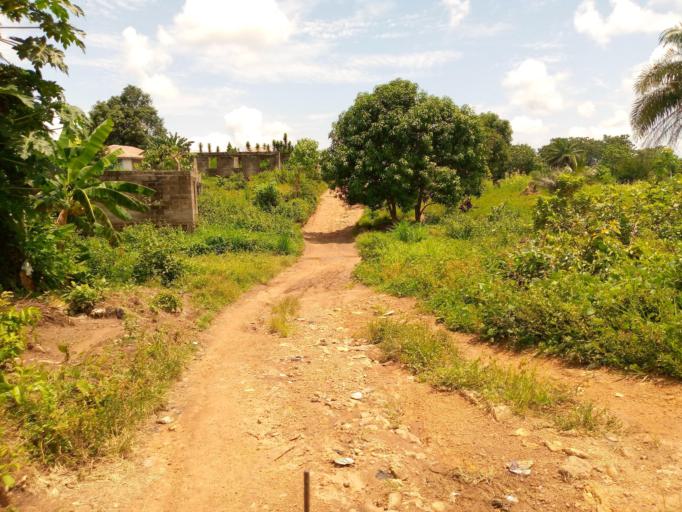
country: SL
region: Northern Province
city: Magburaka
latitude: 8.7318
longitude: -11.9409
